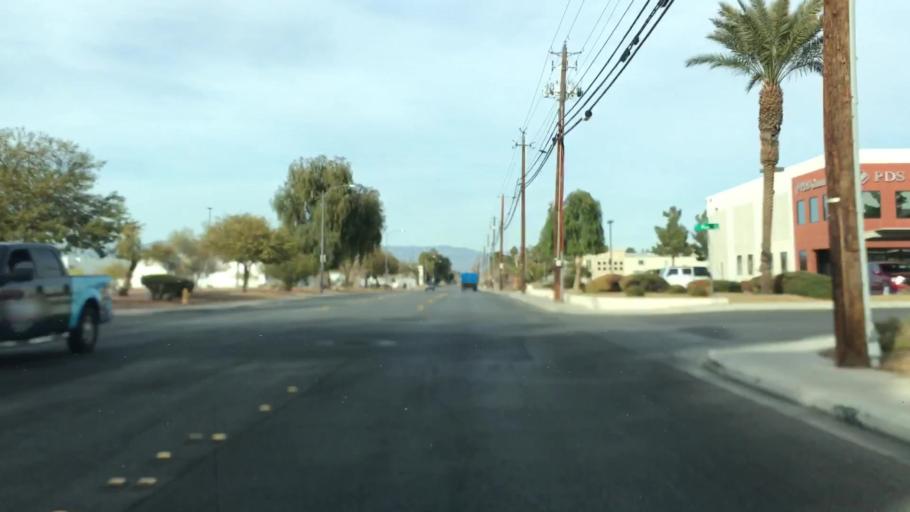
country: US
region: Nevada
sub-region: Clark County
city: Whitney
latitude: 36.0746
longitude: -115.0870
